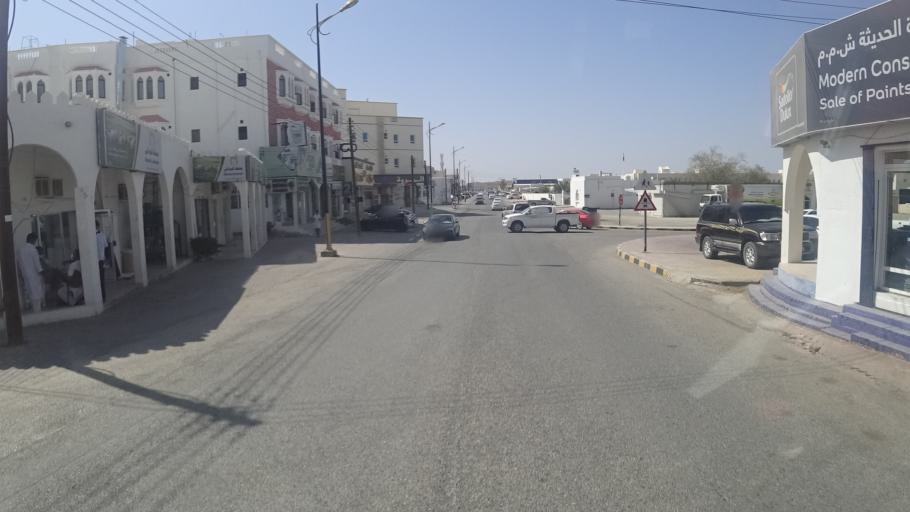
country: OM
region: Ash Sharqiyah
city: Ibra'
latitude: 22.6967
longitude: 58.5463
